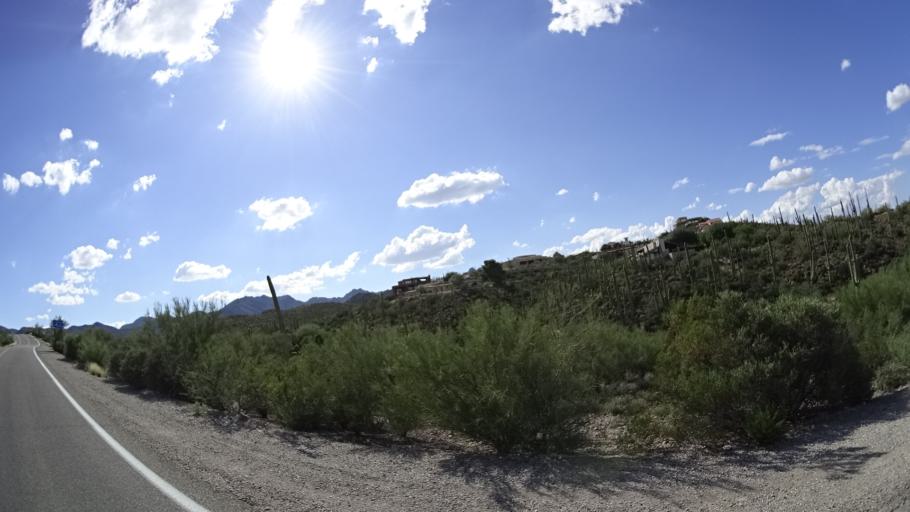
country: US
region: Arizona
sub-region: Pima County
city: Flowing Wells
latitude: 32.2515
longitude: -111.0618
